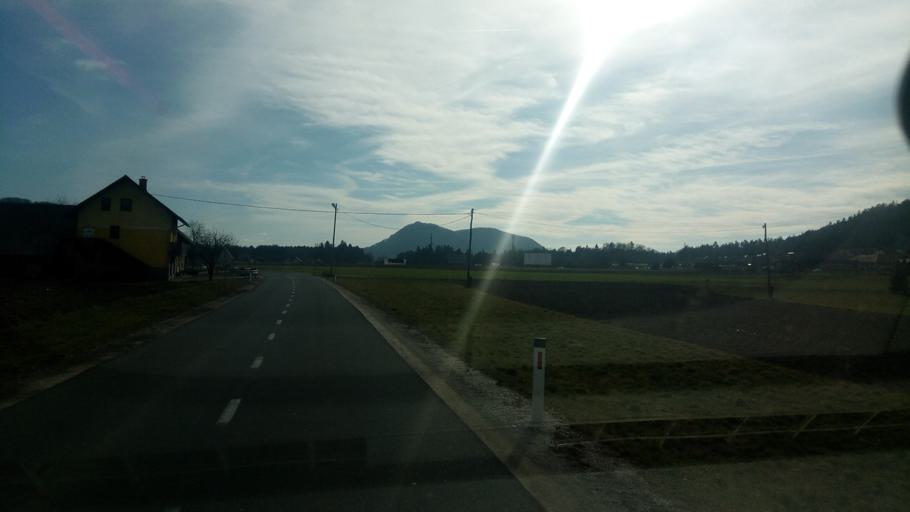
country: SI
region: Vodice
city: Vodice
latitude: 46.1754
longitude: 14.4893
